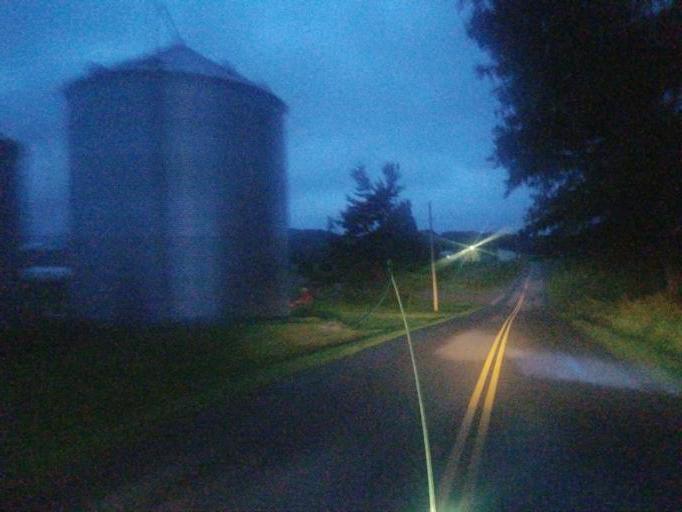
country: US
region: Ohio
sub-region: Carroll County
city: Carrollton
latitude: 40.6232
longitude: -80.9897
